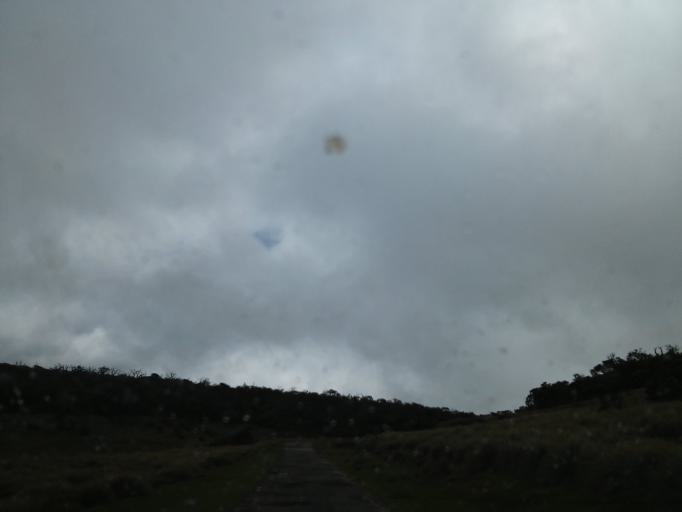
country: LK
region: Uva
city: Haputale
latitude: 6.7947
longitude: 80.8218
